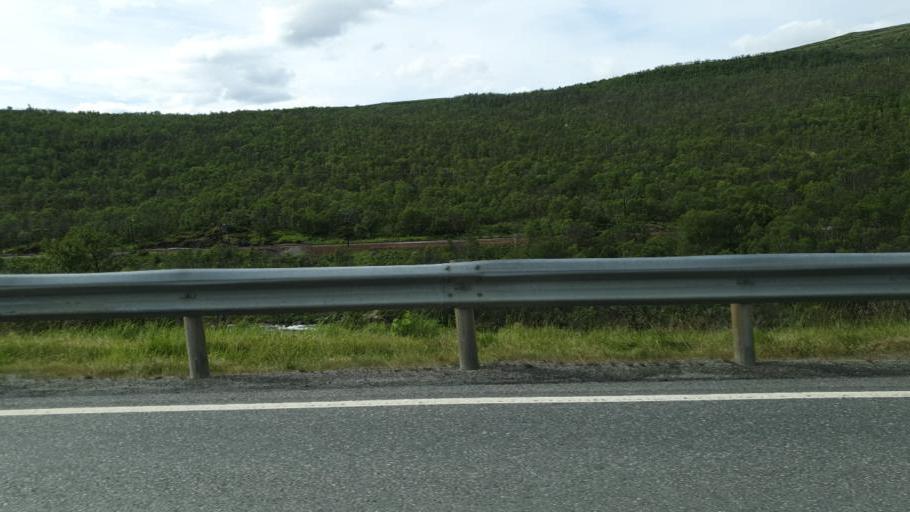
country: NO
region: Sor-Trondelag
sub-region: Oppdal
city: Oppdal
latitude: 62.2988
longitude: 9.5994
